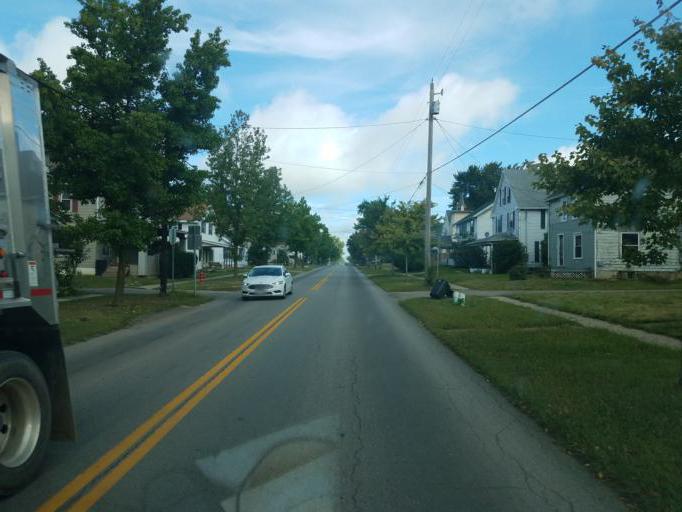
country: US
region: Ohio
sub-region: Wayne County
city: West Salem
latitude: 40.9735
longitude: -82.1097
